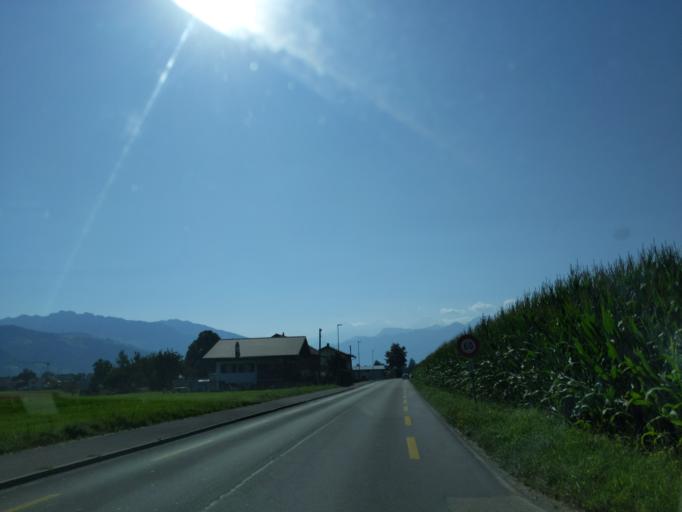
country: CH
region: Bern
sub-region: Thun District
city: Thun
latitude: 46.7364
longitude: 7.6040
